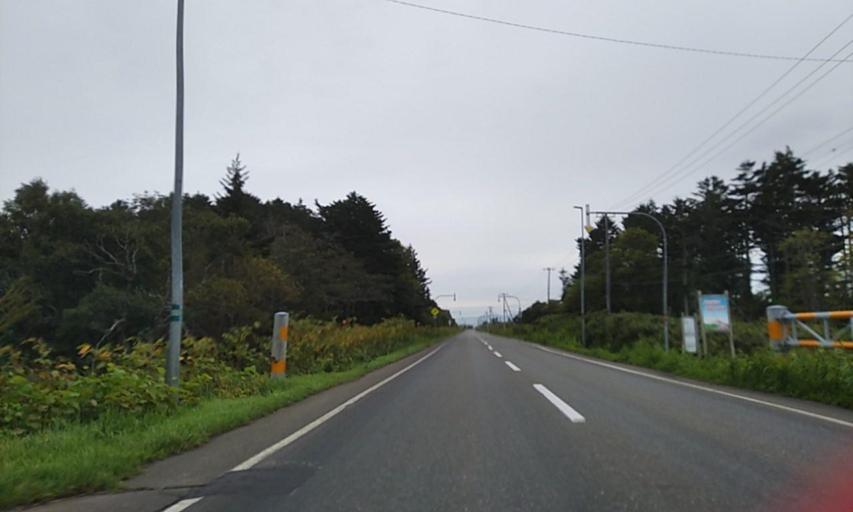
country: JP
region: Hokkaido
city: Makubetsu
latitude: 45.2730
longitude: 142.2302
